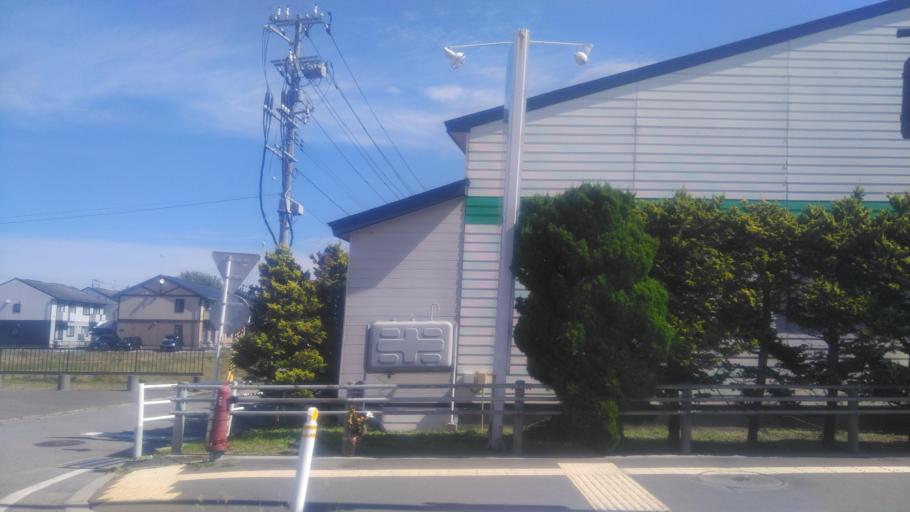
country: JP
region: Akita
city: Noshiromachi
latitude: 40.1989
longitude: 140.0227
